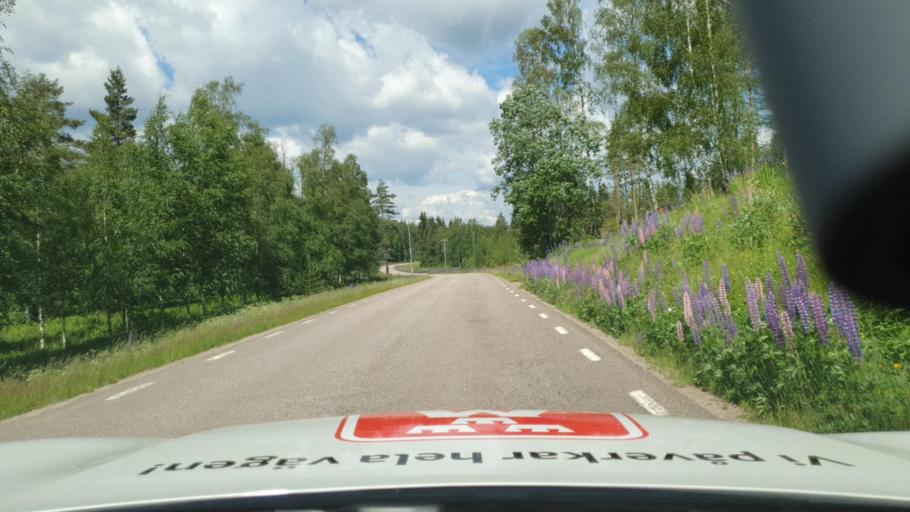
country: SE
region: Vaermland
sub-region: Torsby Kommun
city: Torsby
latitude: 60.4683
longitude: 12.8847
